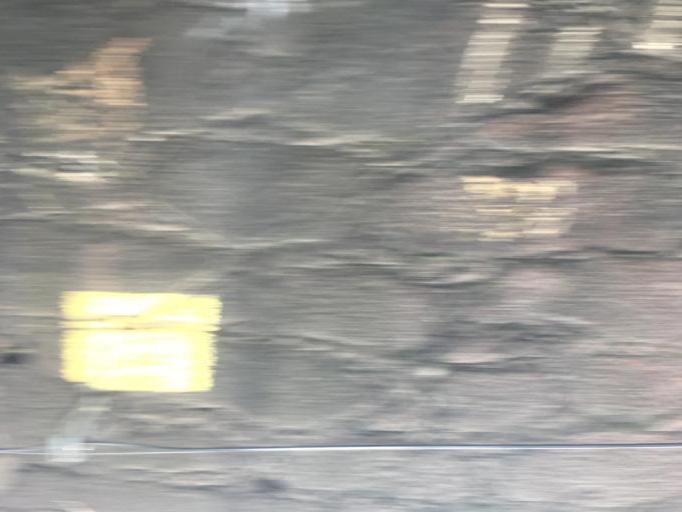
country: BR
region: Rio de Janeiro
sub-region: Rio De Janeiro
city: Rio de Janeiro
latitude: -22.9044
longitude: -43.2727
